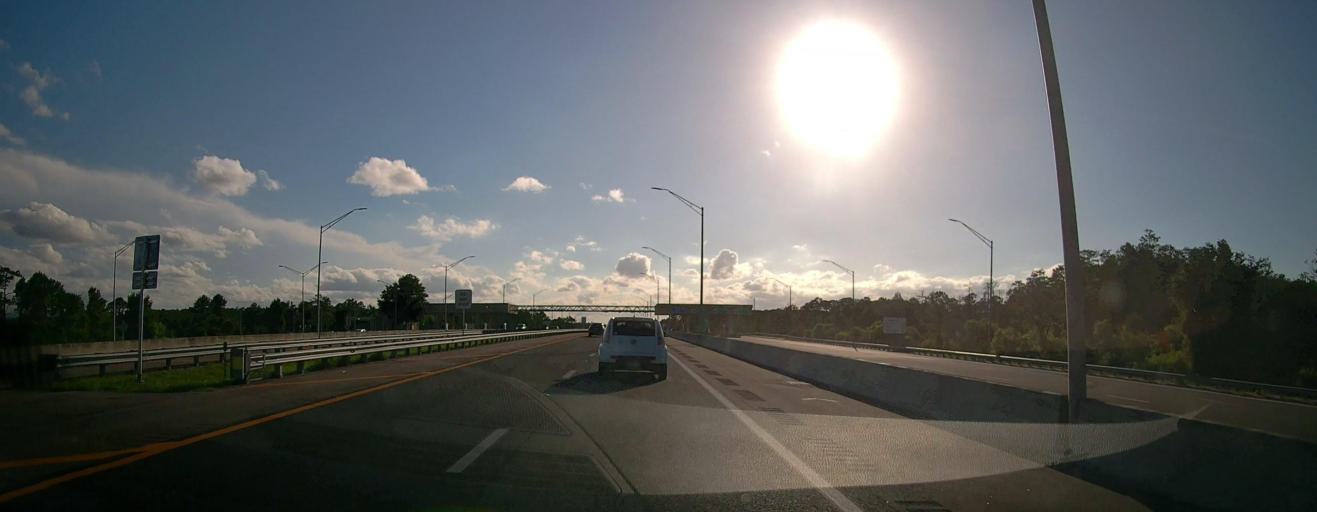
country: US
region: Florida
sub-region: Orange County
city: Alafaya
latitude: 28.4523
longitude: -81.2085
